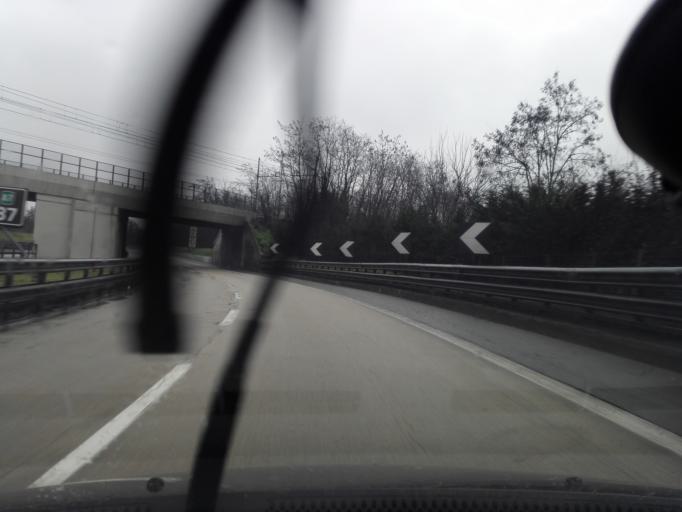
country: IT
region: Piedmont
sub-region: Provincia di Alessandria
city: Serravalle Scrivia
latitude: 44.7136
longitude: 8.8639
